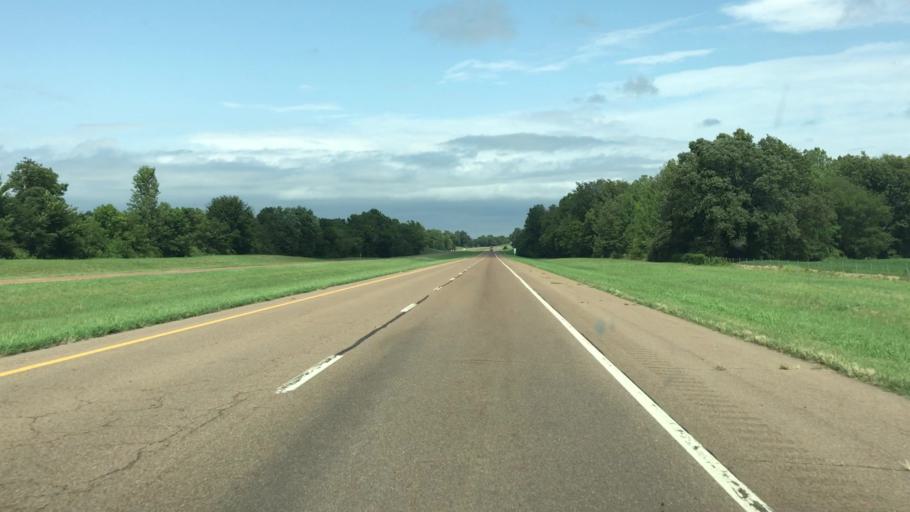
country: US
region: Tennessee
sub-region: Obion County
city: Union City
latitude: 36.4688
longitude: -88.9704
